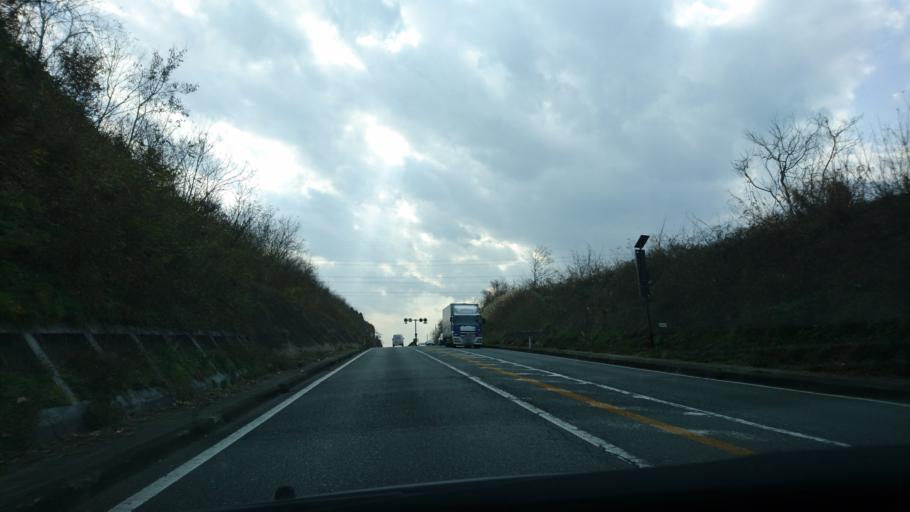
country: JP
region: Iwate
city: Mizusawa
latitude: 39.0277
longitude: 141.1169
